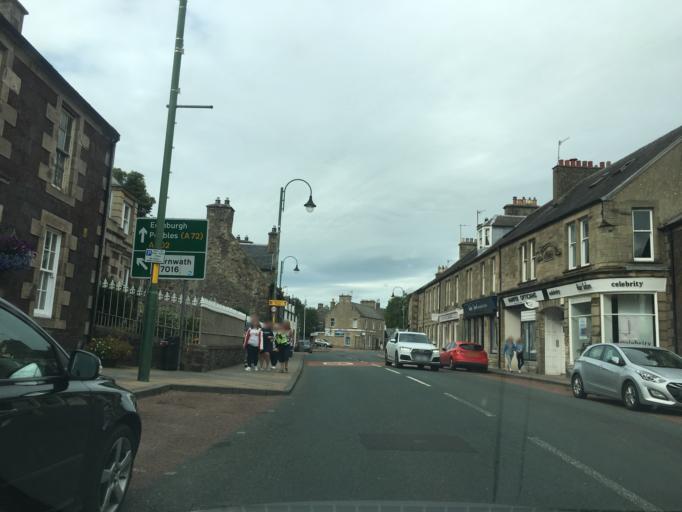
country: GB
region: Scotland
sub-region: South Lanarkshire
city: Biggar
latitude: 55.6230
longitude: -3.5266
